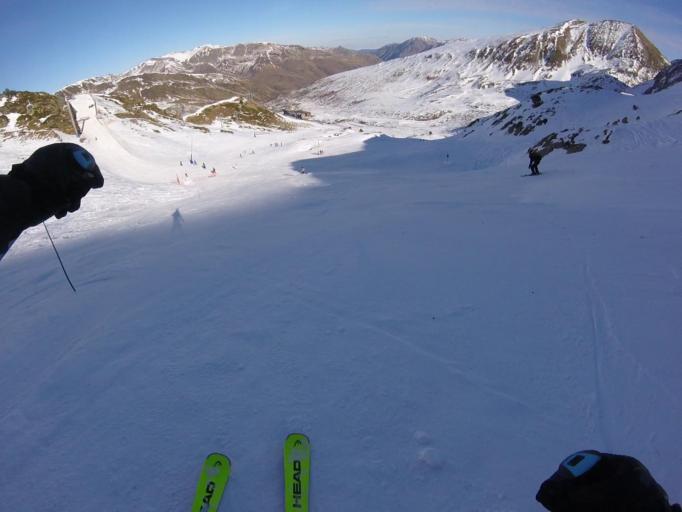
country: AD
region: Encamp
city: Pas de la Casa
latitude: 42.5284
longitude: 1.7263
